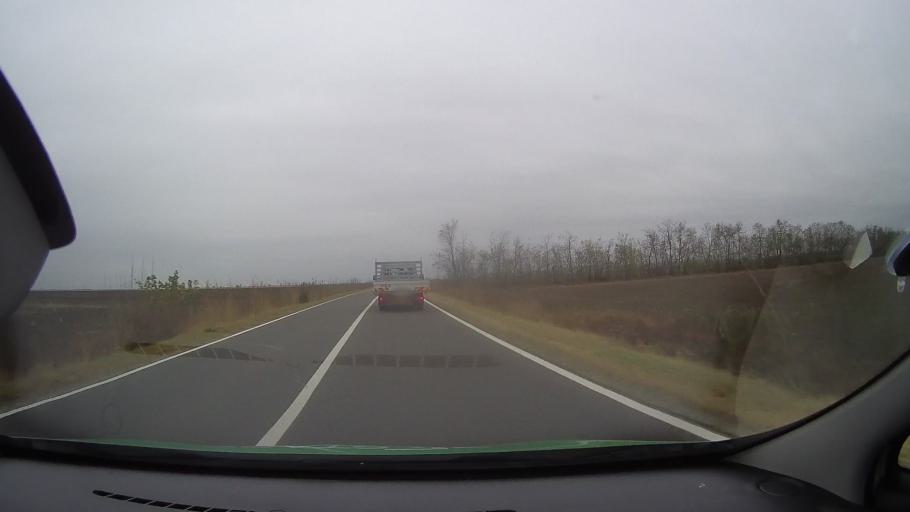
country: RO
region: Ialomita
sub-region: Comuna Gheorghe Lazar
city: Gheorghe Lazar
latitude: 44.6730
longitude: 27.4184
